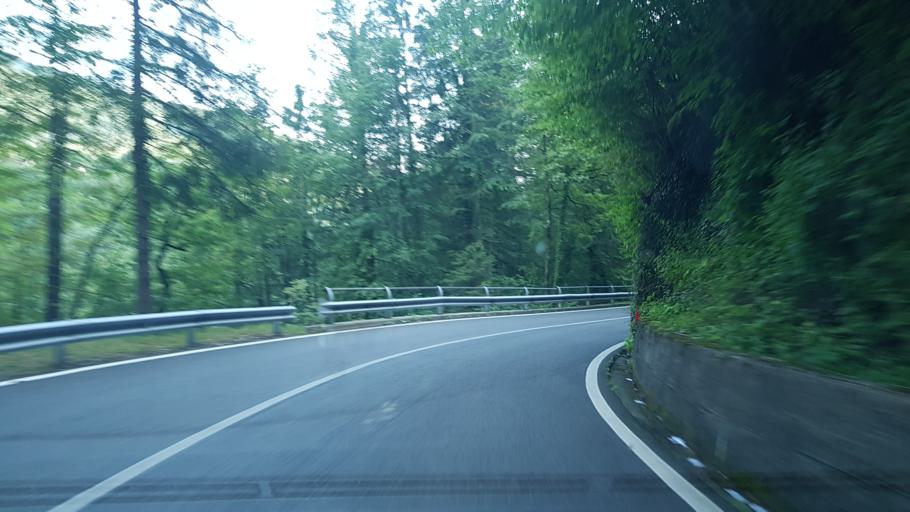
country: IT
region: Friuli Venezia Giulia
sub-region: Provincia di Udine
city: Comeglians
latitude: 46.5265
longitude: 12.8694
